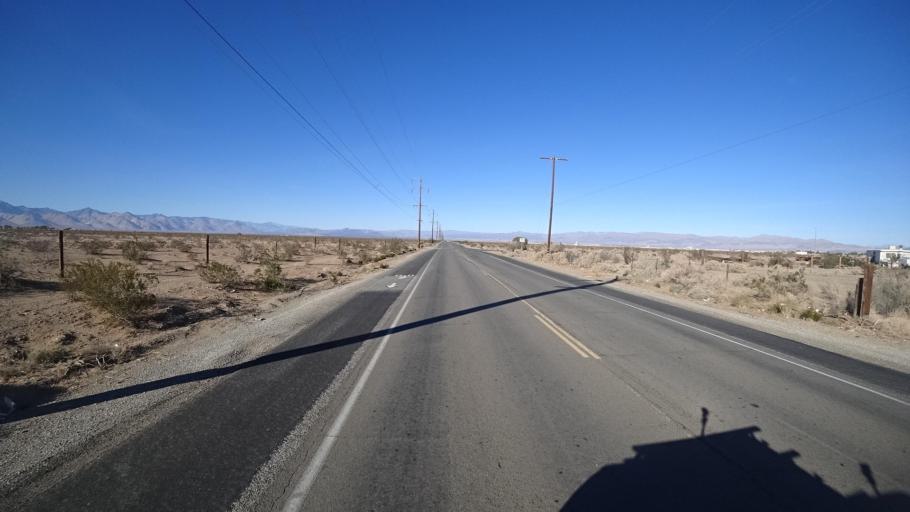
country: US
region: California
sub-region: Kern County
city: China Lake Acres
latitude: 35.6363
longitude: -117.7231
